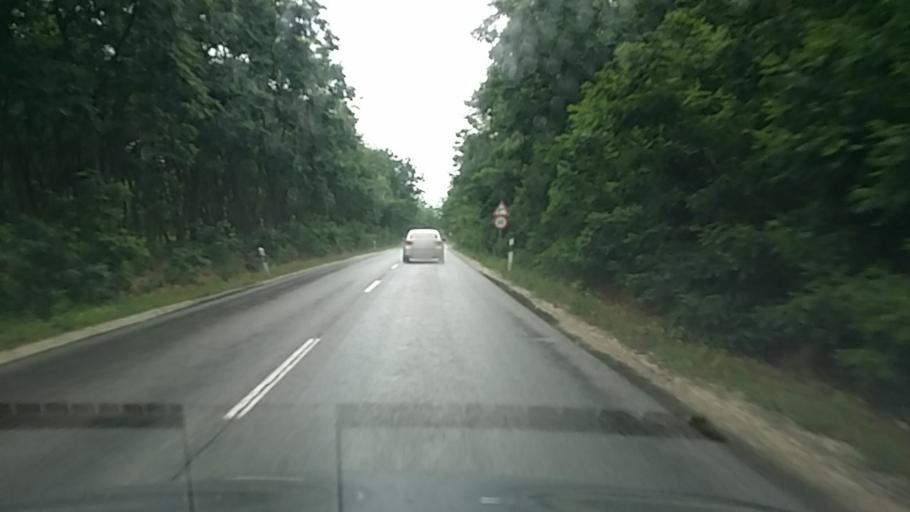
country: HU
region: Pest
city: Ullo
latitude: 47.3484
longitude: 19.3096
